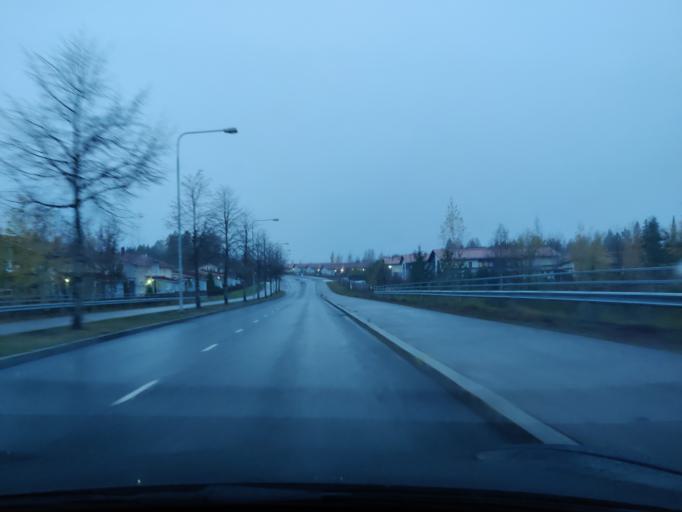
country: FI
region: Northern Savo
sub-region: Kuopio
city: Kuopio
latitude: 62.8260
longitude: 27.6901
